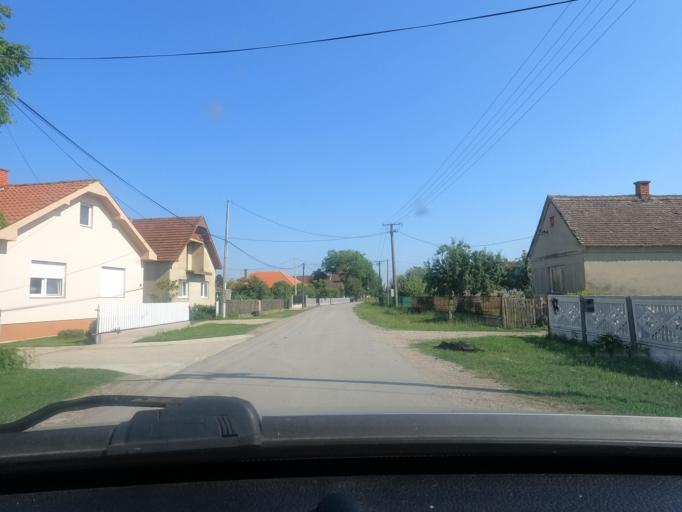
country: RS
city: Bogosavac
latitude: 44.7505
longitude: 19.5813
